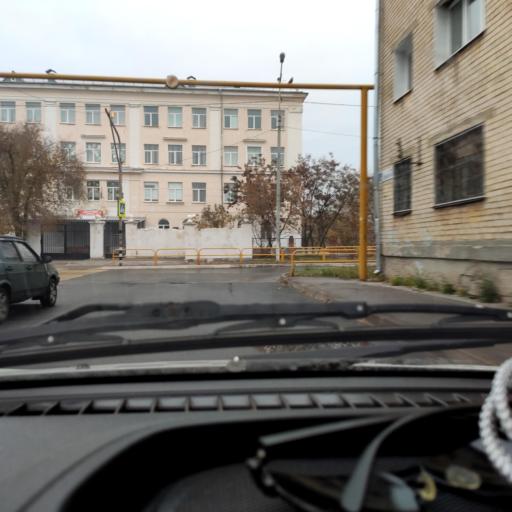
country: RU
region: Samara
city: Zhigulevsk
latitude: 53.4668
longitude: 49.5331
